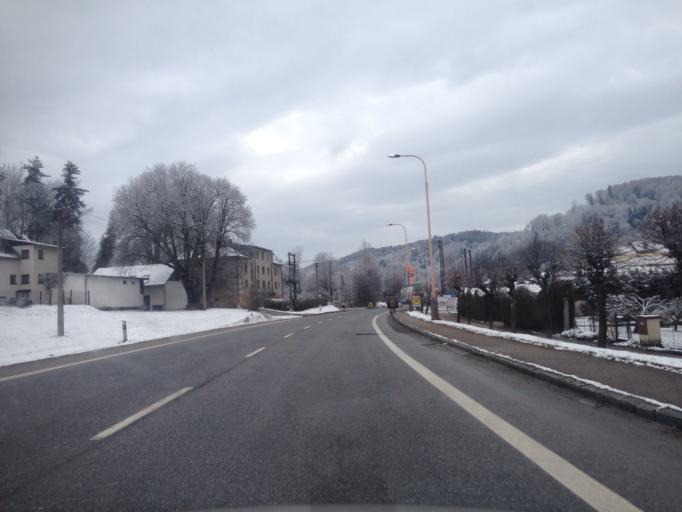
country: CZ
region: Liberecky
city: Jilemnice
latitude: 50.6290
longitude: 15.4784
